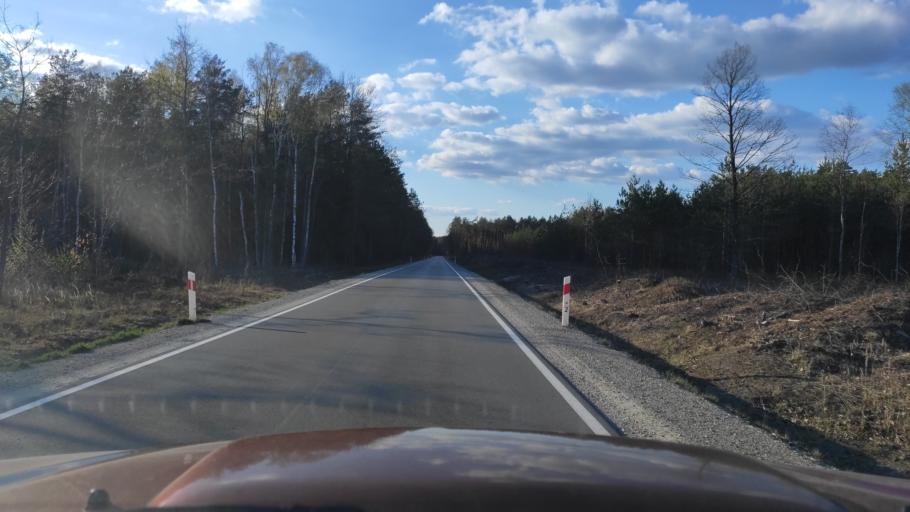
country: PL
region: Masovian Voivodeship
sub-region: Powiat zwolenski
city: Zwolen
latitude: 51.3977
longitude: 21.5411
